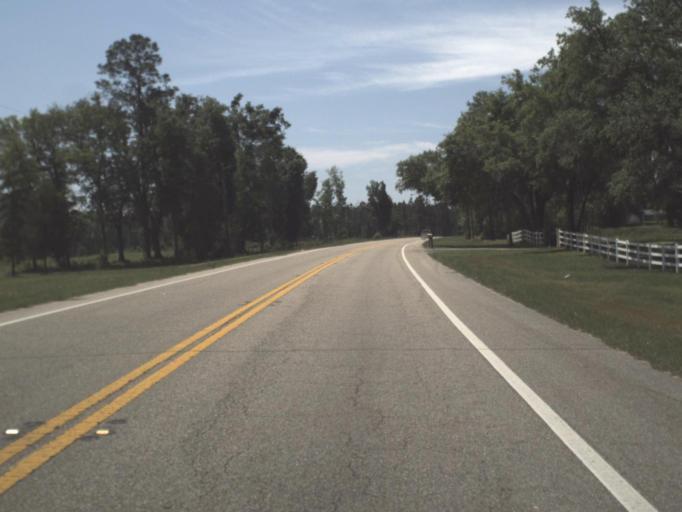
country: US
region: Florida
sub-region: Jackson County
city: Marianna
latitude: 30.6228
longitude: -85.1809
